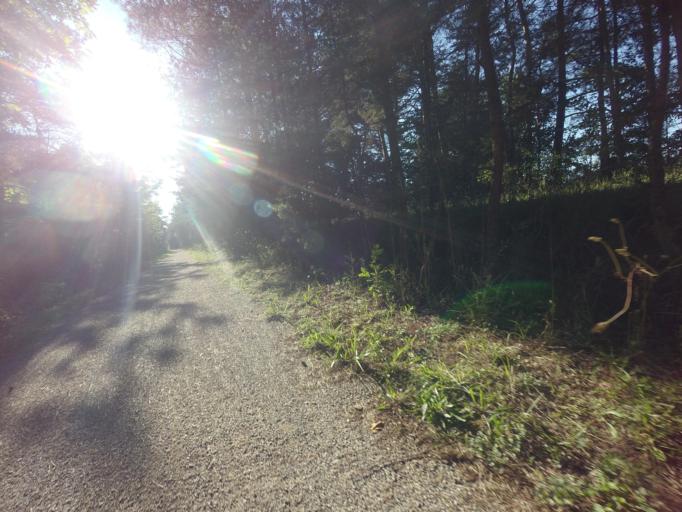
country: CA
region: Ontario
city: Goderich
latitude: 43.7535
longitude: -81.6048
